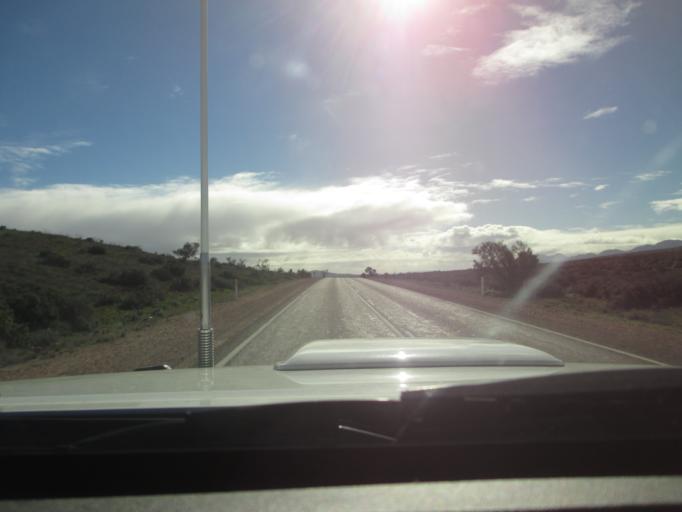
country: AU
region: South Australia
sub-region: Flinders Ranges
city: Quorn
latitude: -31.7407
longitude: 138.3388
